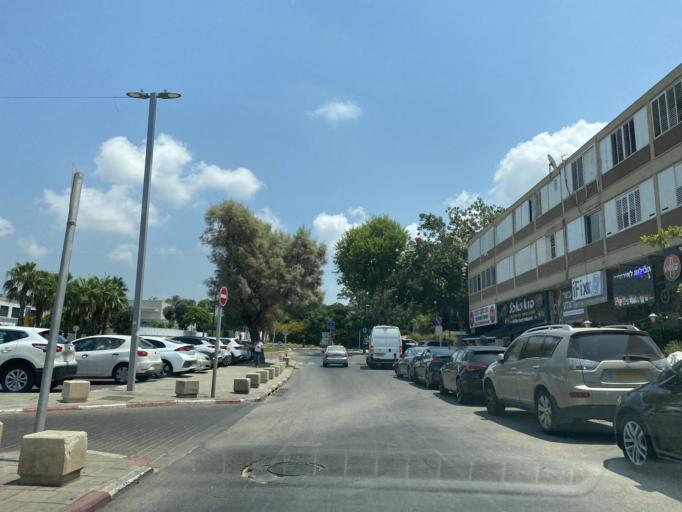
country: IL
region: Tel Aviv
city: Herzliya Pituah
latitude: 32.1790
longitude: 34.8052
